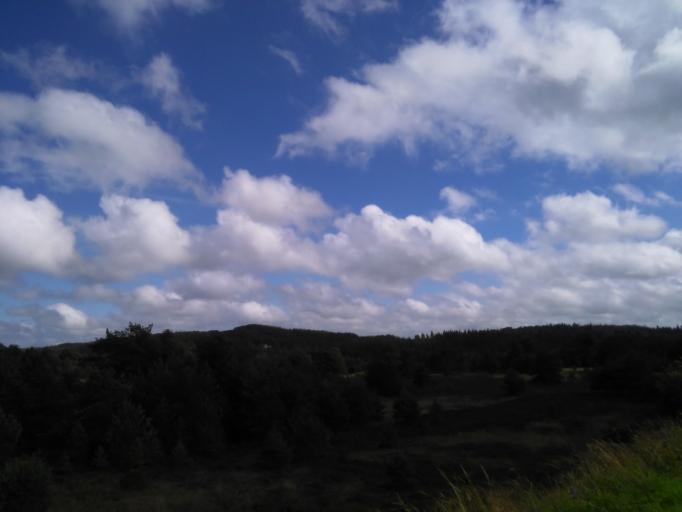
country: DK
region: Central Jutland
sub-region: Silkeborg Kommune
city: Virklund
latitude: 56.0527
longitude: 9.4724
